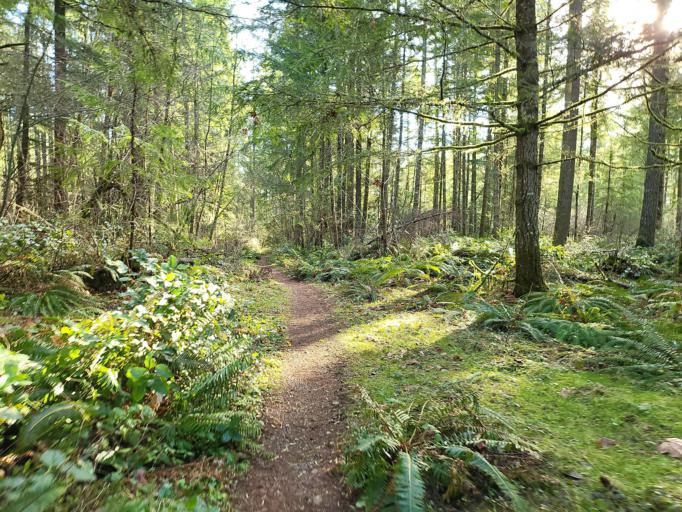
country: US
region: Washington
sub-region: King County
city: Issaquah
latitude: 47.5218
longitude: -122.0210
